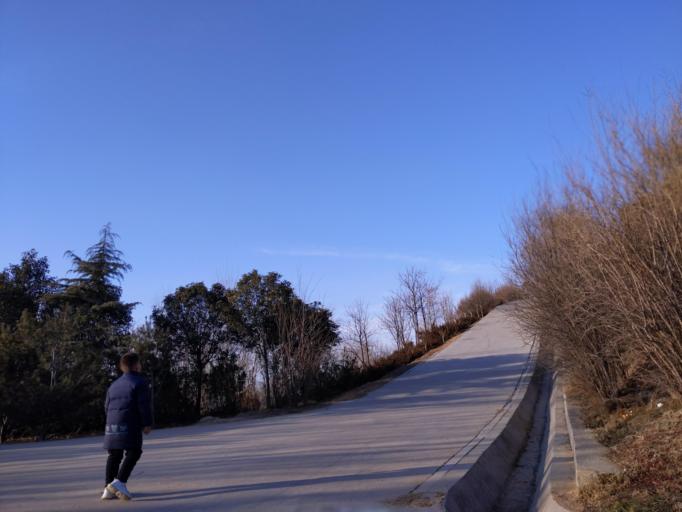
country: CN
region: Henan Sheng
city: Puyang
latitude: 35.7668
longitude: 114.9957
